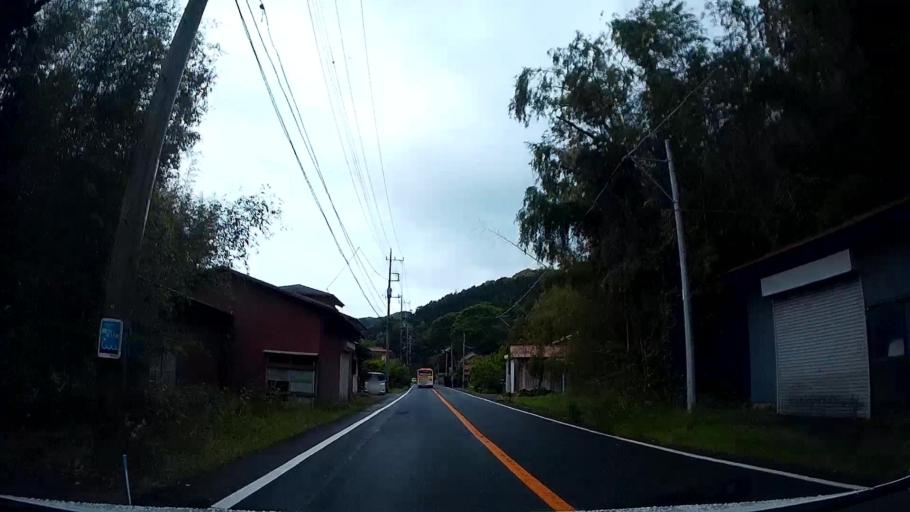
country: JP
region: Shizuoka
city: Shimoda
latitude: 34.7675
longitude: 138.9740
